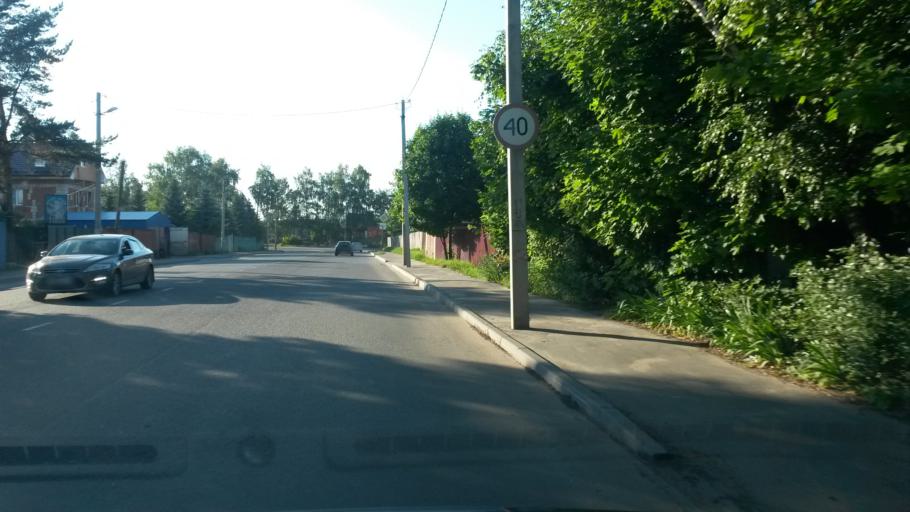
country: RU
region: Ivanovo
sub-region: Gorod Ivanovo
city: Ivanovo
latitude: 57.0191
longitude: 40.9230
